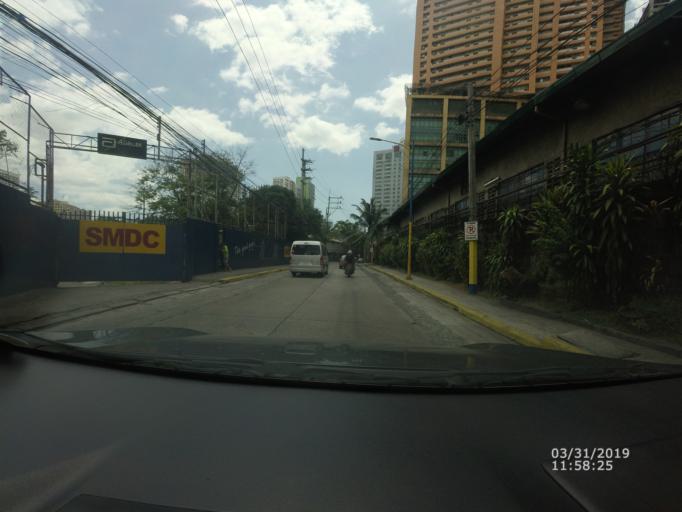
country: PH
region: Metro Manila
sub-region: Mandaluyong
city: Mandaluyong City
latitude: 14.5731
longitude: 121.0501
